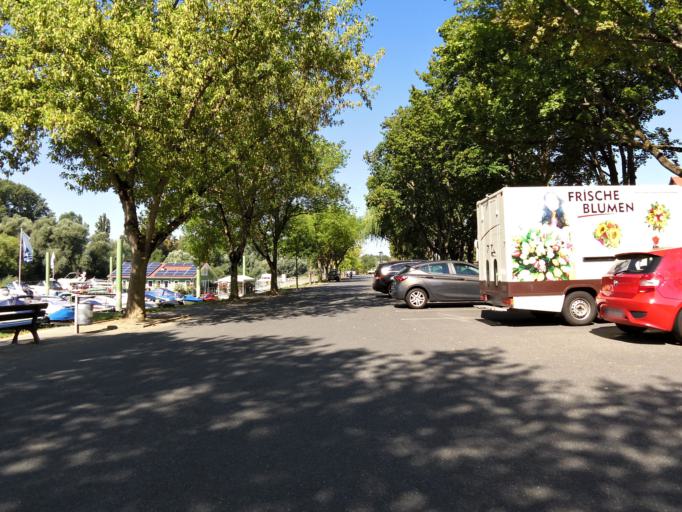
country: DE
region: Hesse
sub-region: Regierungsbezirk Darmstadt
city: Ginsheim-Gustavsburg
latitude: 49.9626
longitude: 8.3455
